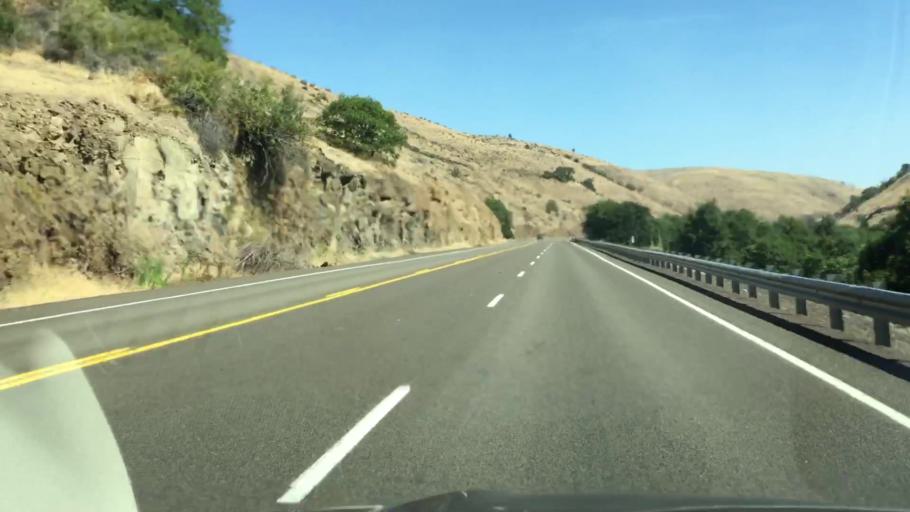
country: US
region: Oregon
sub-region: Wasco County
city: The Dalles
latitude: 45.2840
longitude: -121.1856
